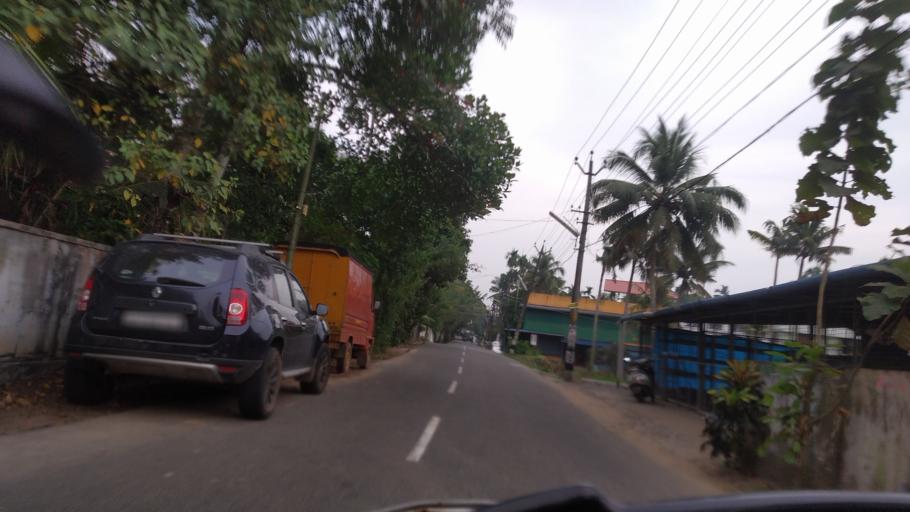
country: IN
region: Kerala
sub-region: Ernakulam
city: Elur
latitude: 10.1384
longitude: 76.2465
